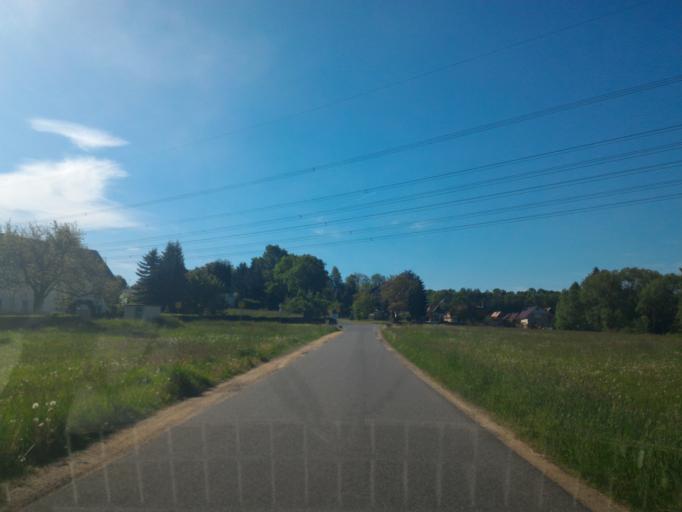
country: DE
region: Saxony
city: Niedercunnersdorf
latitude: 51.0416
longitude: 14.6649
